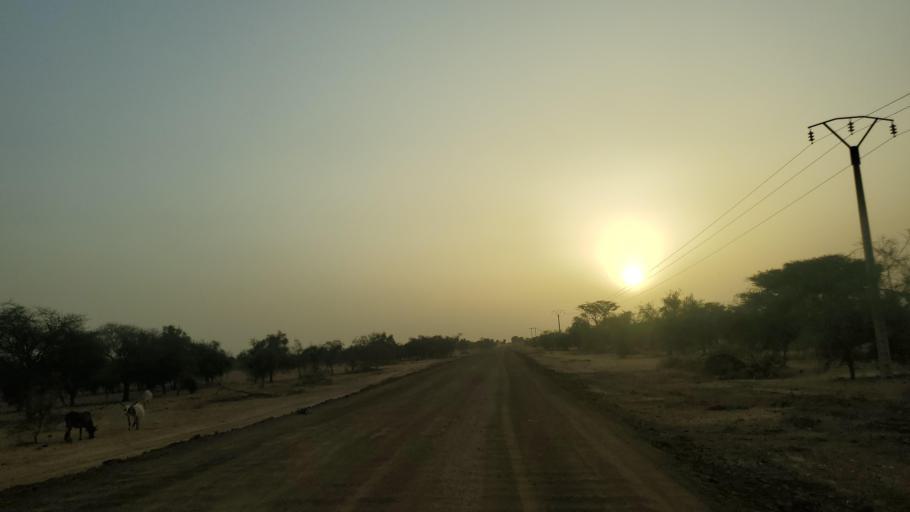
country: SN
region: Louga
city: Dara
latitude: 15.4134
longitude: -15.7022
